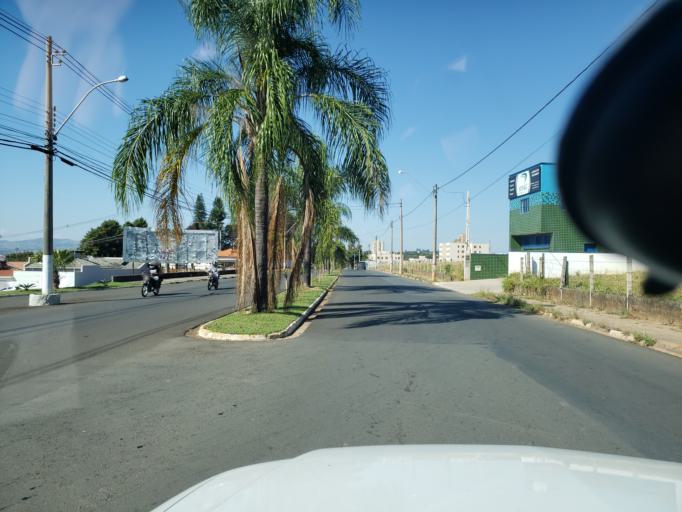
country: BR
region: Sao Paulo
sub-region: Itapira
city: Itapira
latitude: -22.4216
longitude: -46.8386
